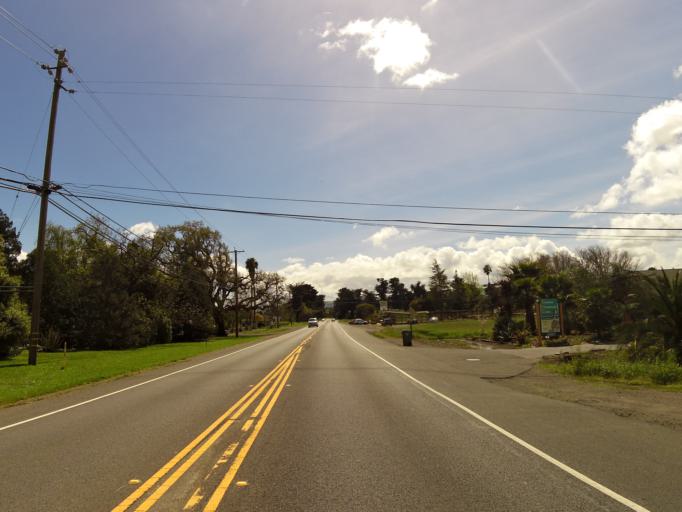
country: US
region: California
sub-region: Sonoma County
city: Sonoma
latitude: 38.2684
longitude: -122.4615
